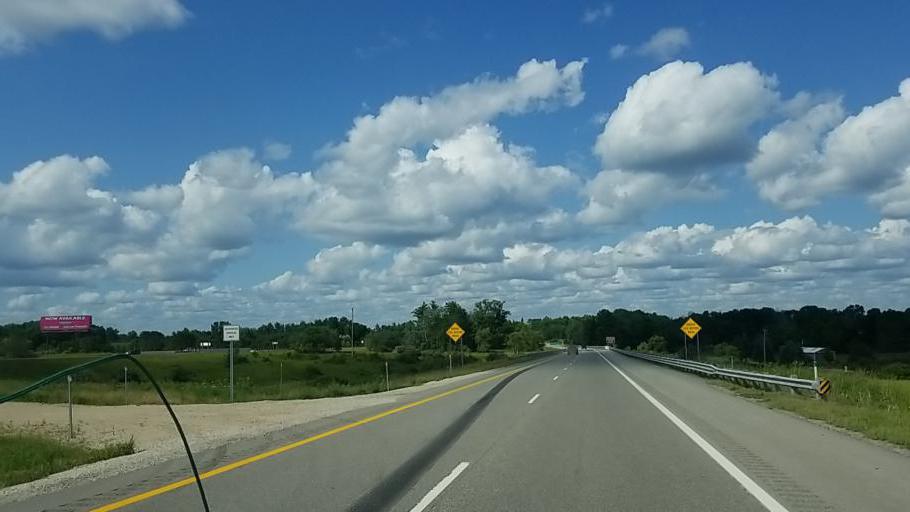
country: US
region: Michigan
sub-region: Osceola County
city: Reed City
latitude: 43.8711
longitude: -85.5305
